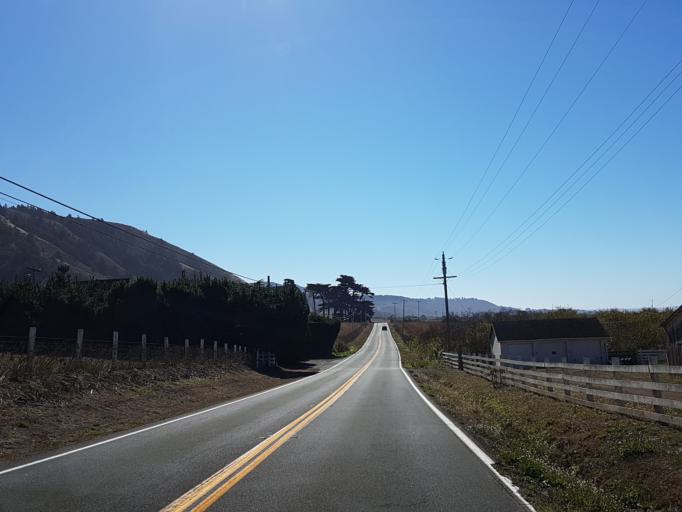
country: US
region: California
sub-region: Mendocino County
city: Boonville
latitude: 39.0805
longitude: -123.6964
